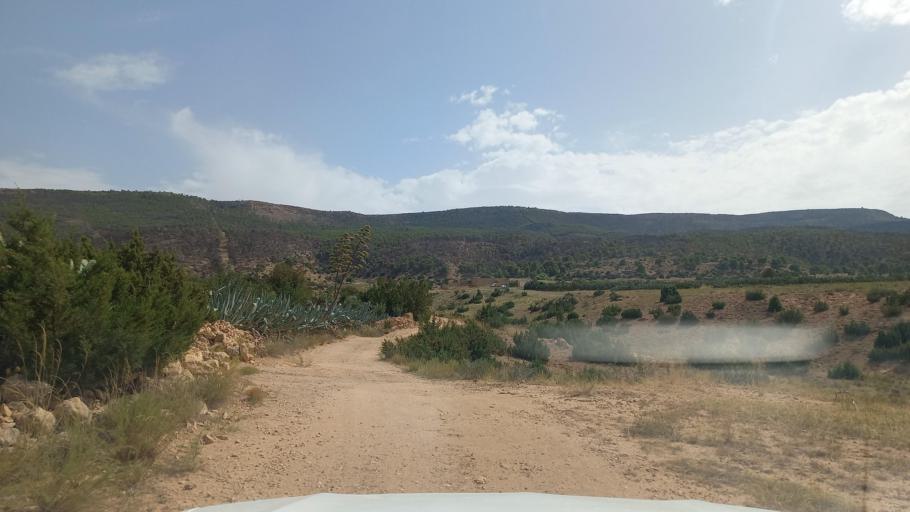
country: TN
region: Al Qasrayn
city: Kasserine
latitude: 35.3580
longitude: 8.8881
